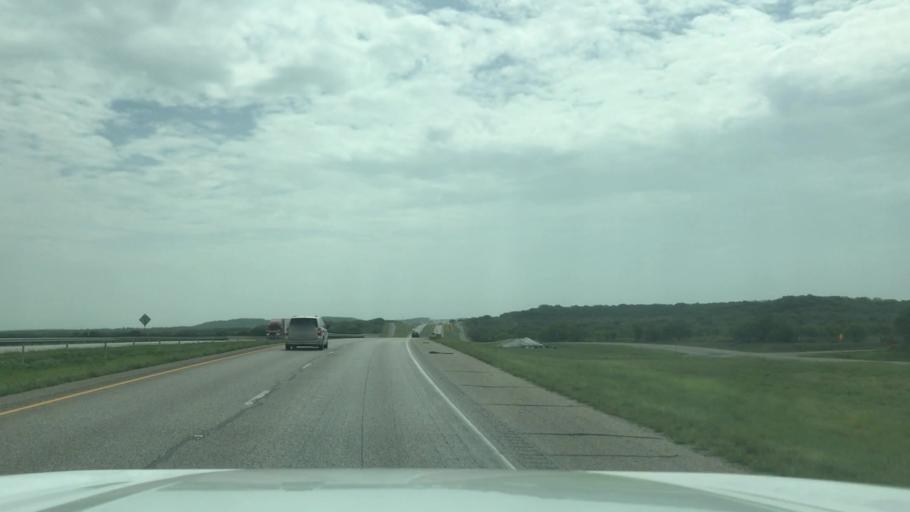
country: US
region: Texas
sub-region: Eastland County
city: Cisco
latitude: 32.3797
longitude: -99.1443
